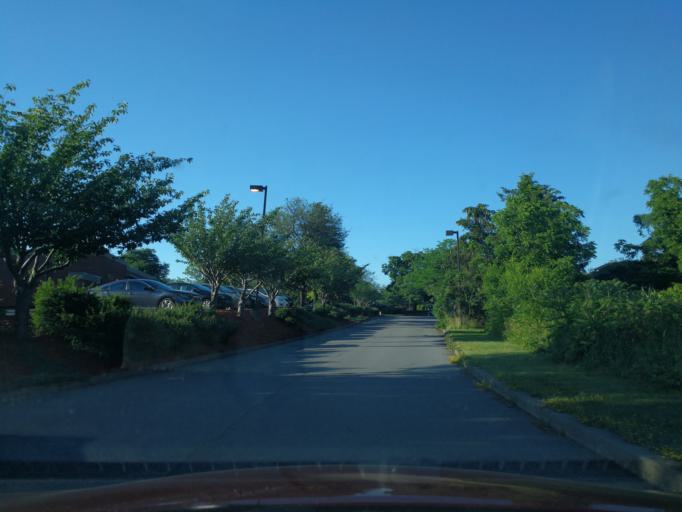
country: US
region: New York
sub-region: Monroe County
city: Greece
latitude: 43.2050
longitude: -77.6733
